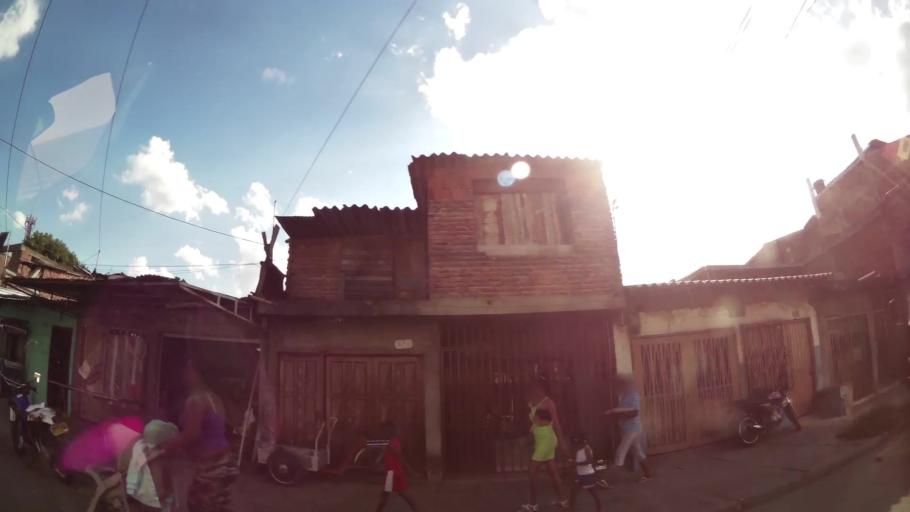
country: CO
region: Valle del Cauca
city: Cali
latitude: 3.4154
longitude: -76.4972
